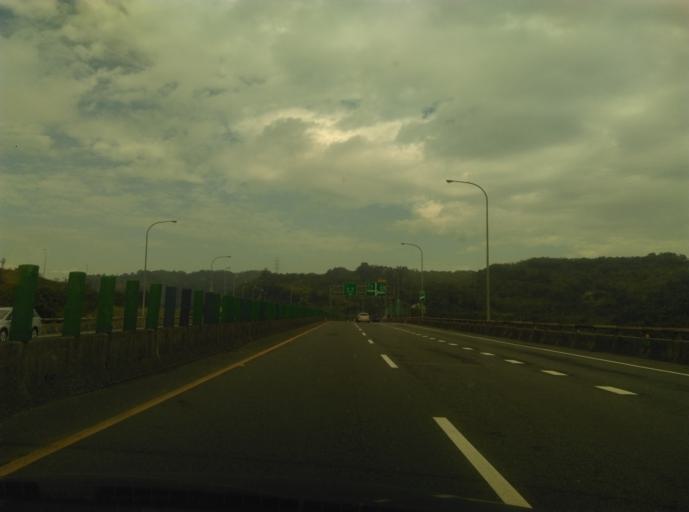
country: TW
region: Taiwan
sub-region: Keelung
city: Keelung
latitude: 25.1216
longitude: 121.6978
